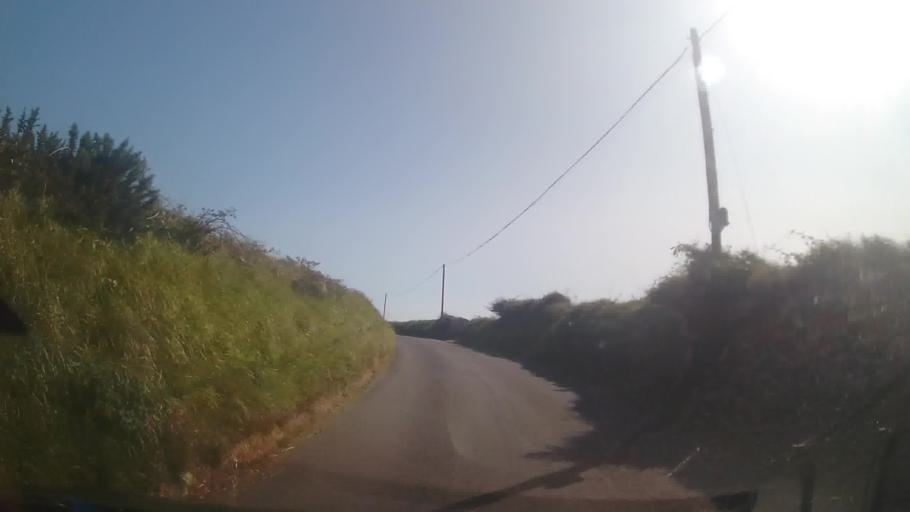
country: GB
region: Wales
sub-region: Pembrokeshire
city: Llanrhian
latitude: 51.9348
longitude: -5.1699
